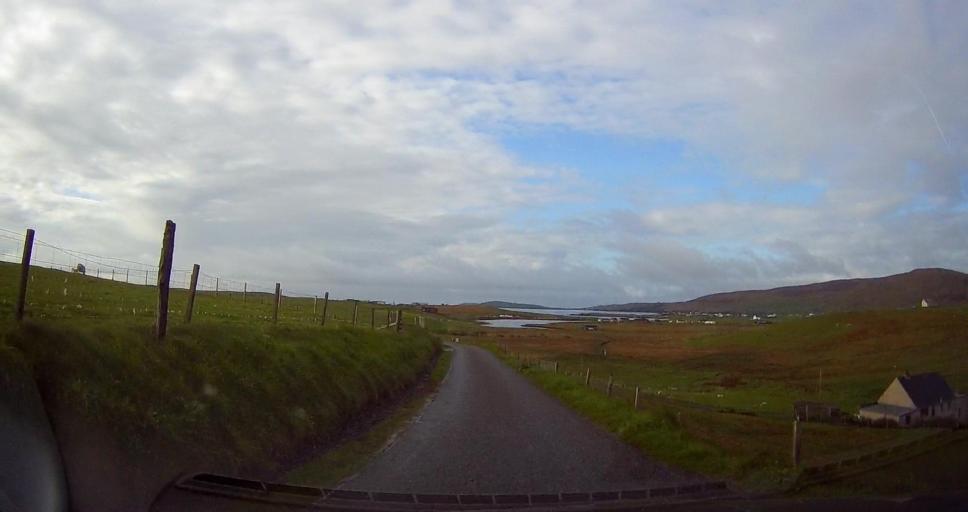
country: GB
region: Scotland
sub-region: Shetland Islands
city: Sandwick
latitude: 60.0531
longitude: -1.2078
